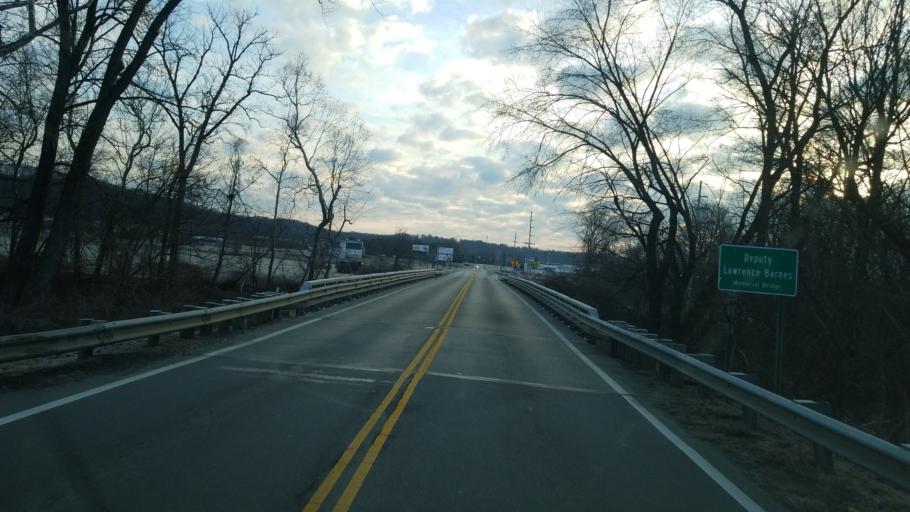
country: US
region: Ohio
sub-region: Ross County
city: North Fork Village
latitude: 39.3505
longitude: -83.0540
